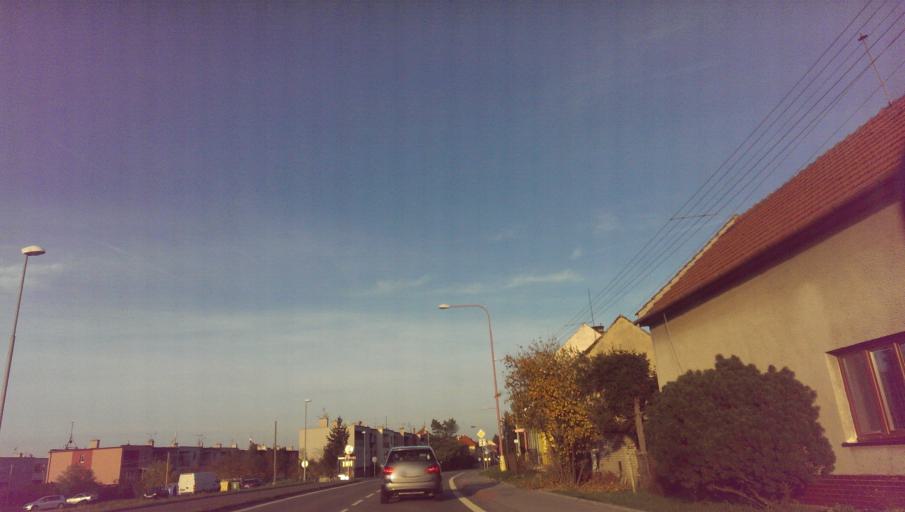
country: CZ
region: Zlin
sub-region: Okres Uherske Hradiste
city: Uherske Hradiste
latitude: 49.0815
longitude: 17.4886
